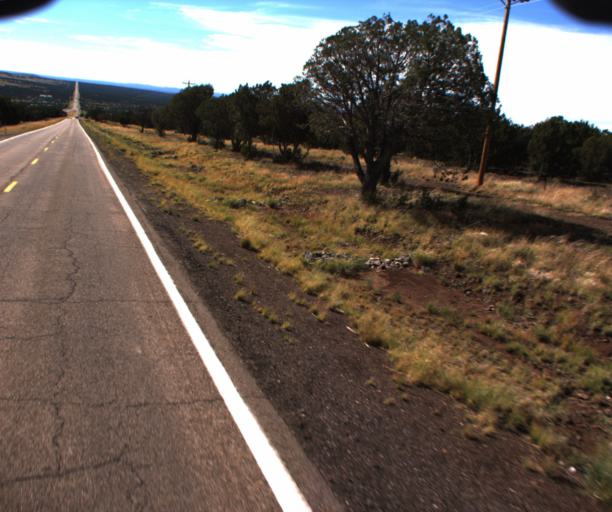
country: US
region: Arizona
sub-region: Navajo County
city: White Mountain Lake
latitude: 34.2890
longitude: -109.8193
